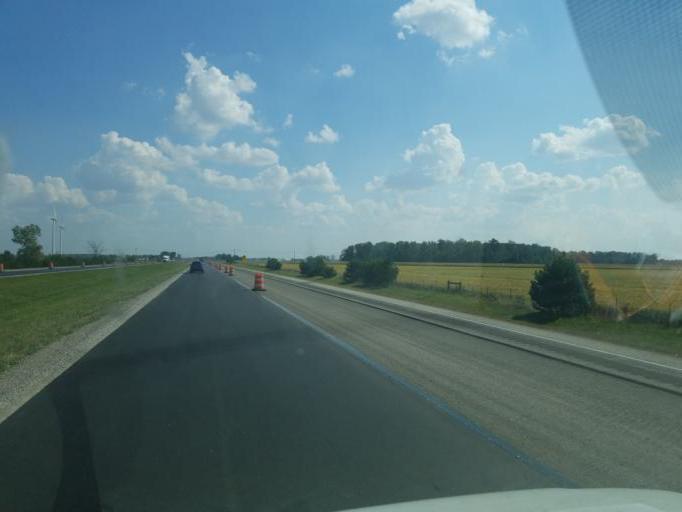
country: US
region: Ohio
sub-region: Van Wert County
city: Convoy
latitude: 40.9197
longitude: -84.6767
